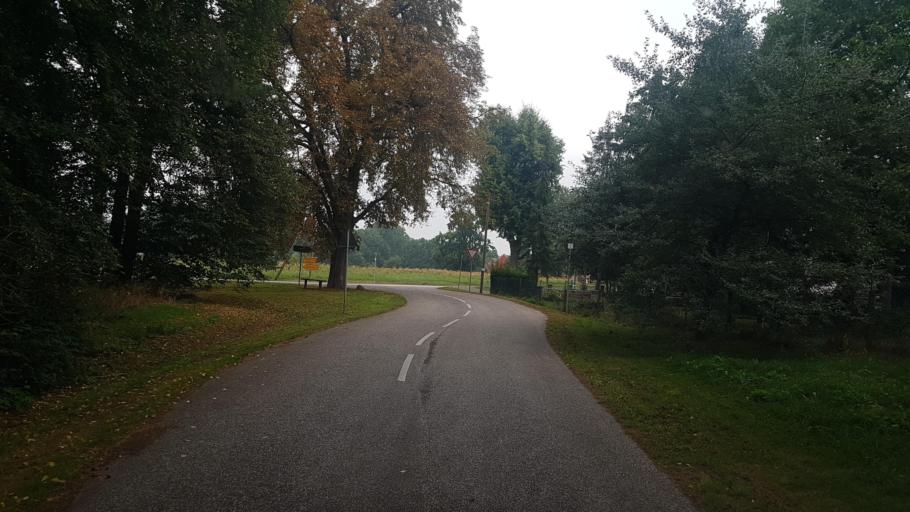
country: DE
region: Brandenburg
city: Niemegk
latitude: 52.0510
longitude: 12.6617
